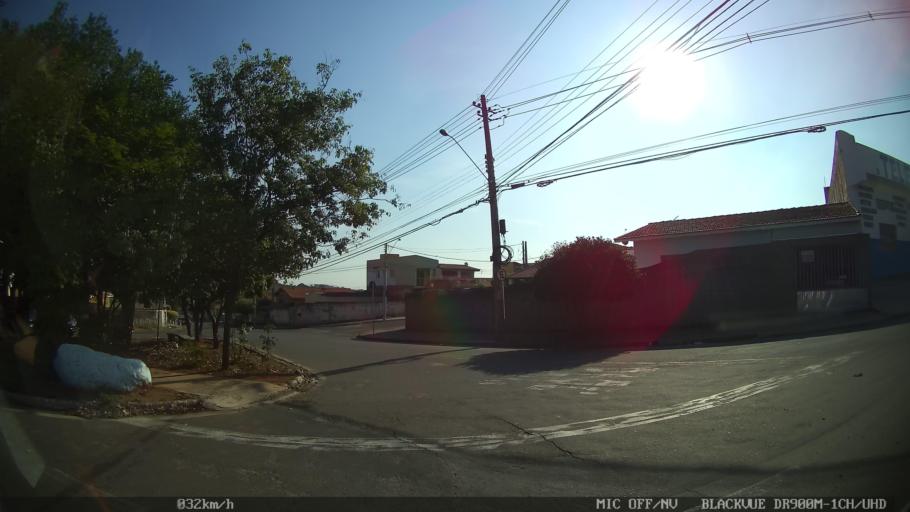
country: BR
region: Sao Paulo
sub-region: Campinas
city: Campinas
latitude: -22.9860
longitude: -47.1488
